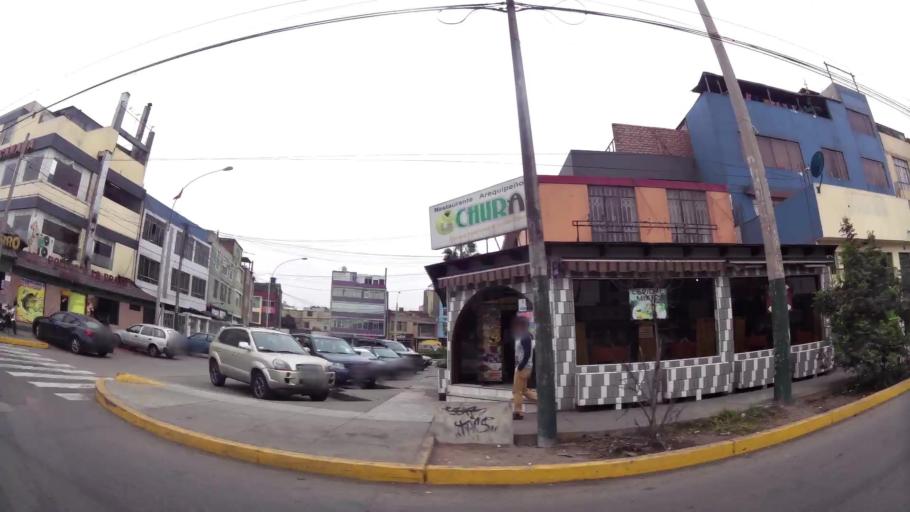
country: PE
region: Lima
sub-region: Lima
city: San Luis
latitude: -12.0816
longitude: -77.0177
